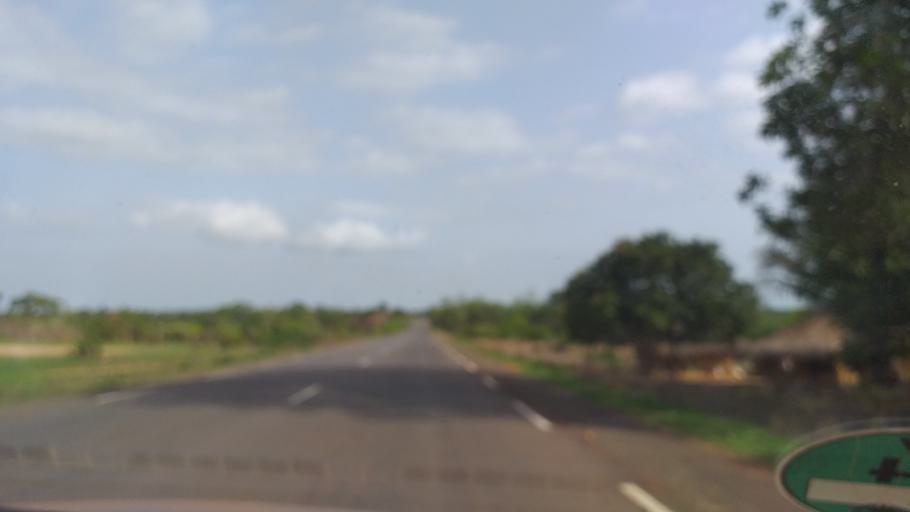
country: GN
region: Boke
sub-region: Boke Prefecture
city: Sangueya
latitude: 10.4446
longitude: -14.4038
